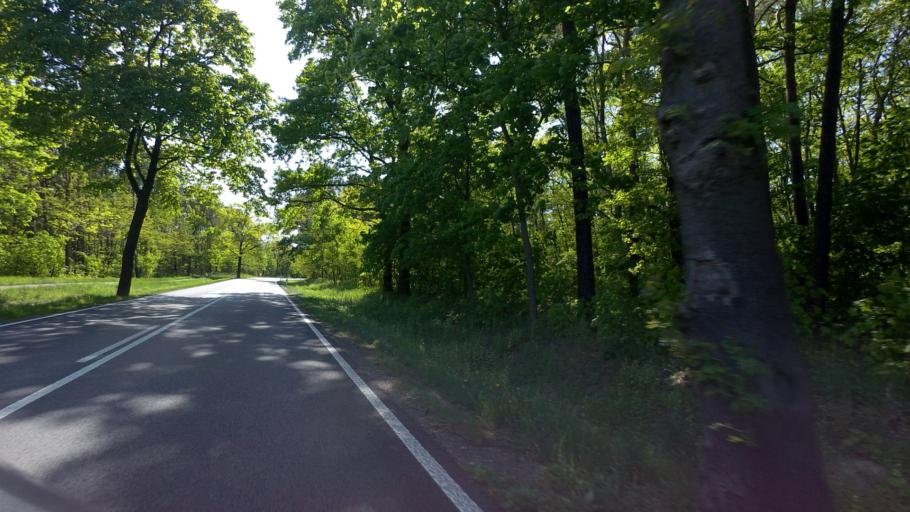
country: DE
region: Brandenburg
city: Tauche
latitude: 52.0699
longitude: 14.1526
